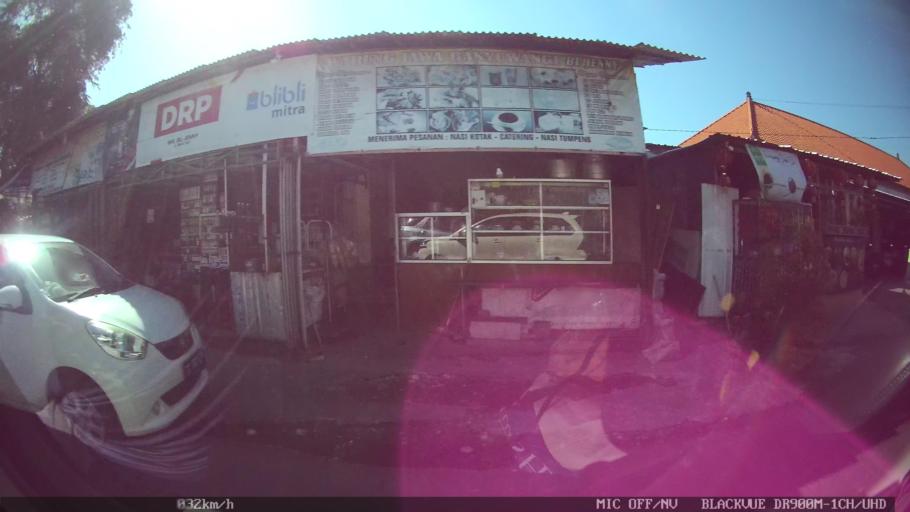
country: ID
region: Bali
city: Banjar Kertasari
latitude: -8.6346
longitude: 115.1848
